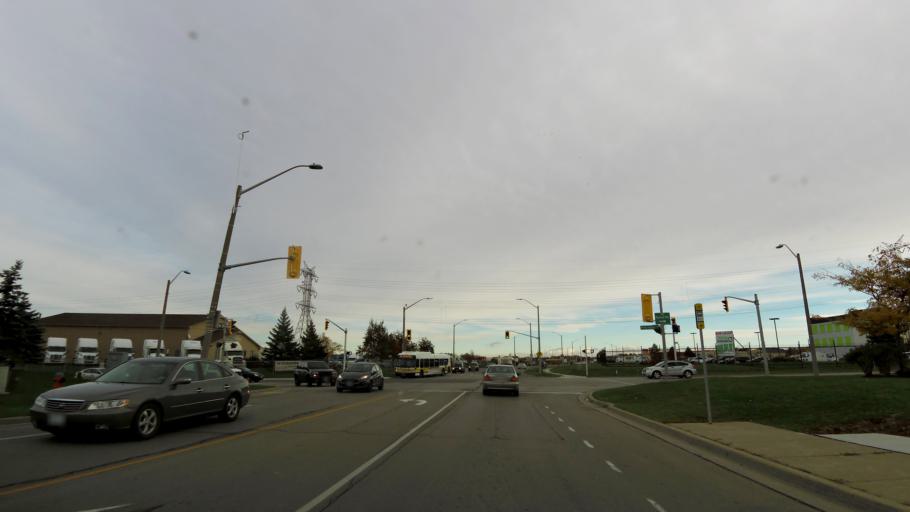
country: CA
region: Ontario
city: Hamilton
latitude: 43.1943
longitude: -79.8197
